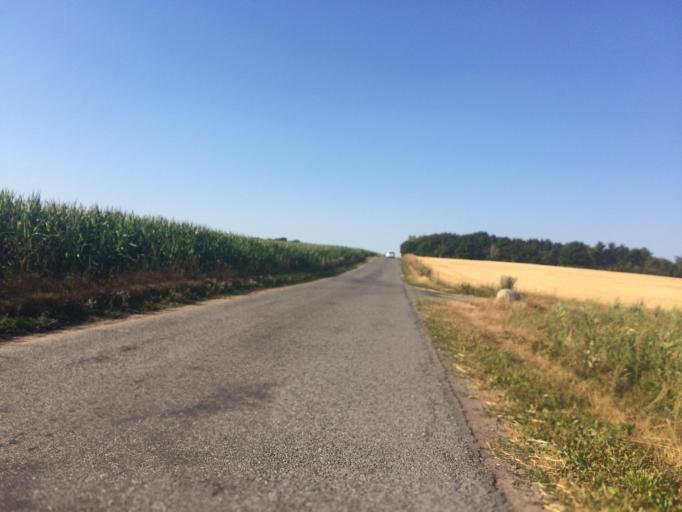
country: DK
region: Central Jutland
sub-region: Holstebro Kommune
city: Vinderup
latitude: 56.5902
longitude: 8.7379
